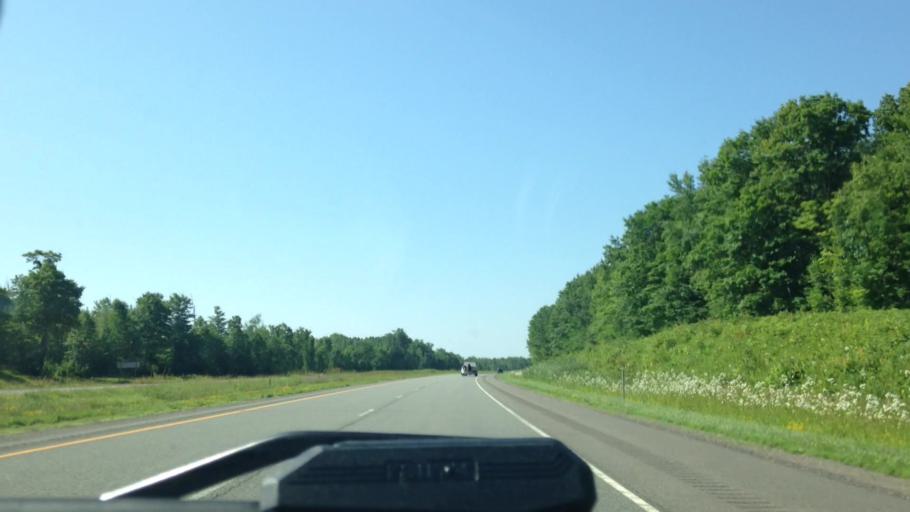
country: US
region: Wisconsin
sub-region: Douglas County
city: Lake Nebagamon
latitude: 46.4159
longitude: -91.8103
